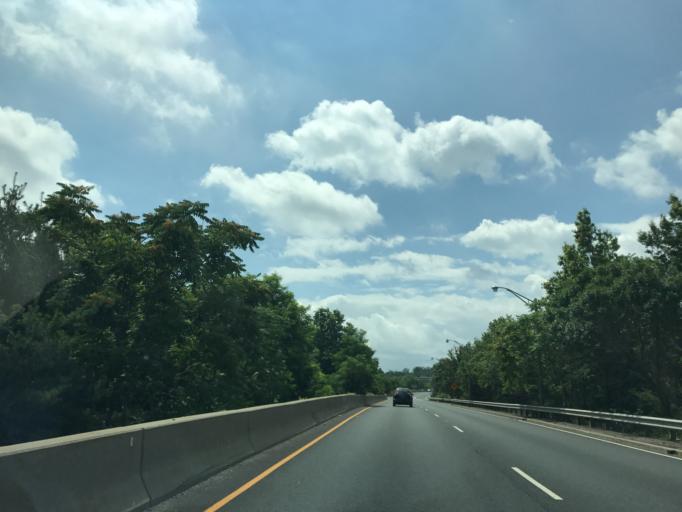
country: US
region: New Jersey
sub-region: Morris County
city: Morris Plains
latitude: 40.8101
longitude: -74.4478
